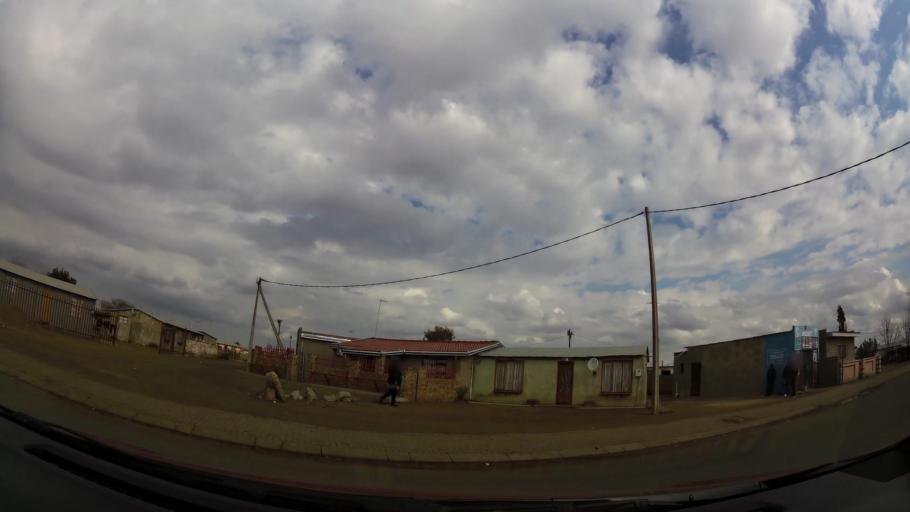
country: ZA
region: Gauteng
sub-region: Sedibeng District Municipality
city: Vanderbijlpark
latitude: -26.6973
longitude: 27.7935
